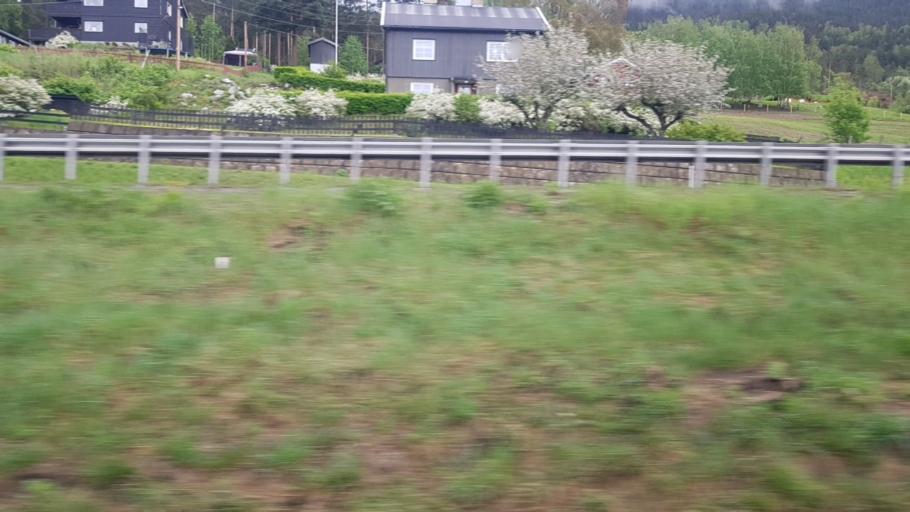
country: NO
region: Oppland
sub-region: Nord-Fron
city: Vinstra
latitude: 61.6061
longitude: 9.7093
